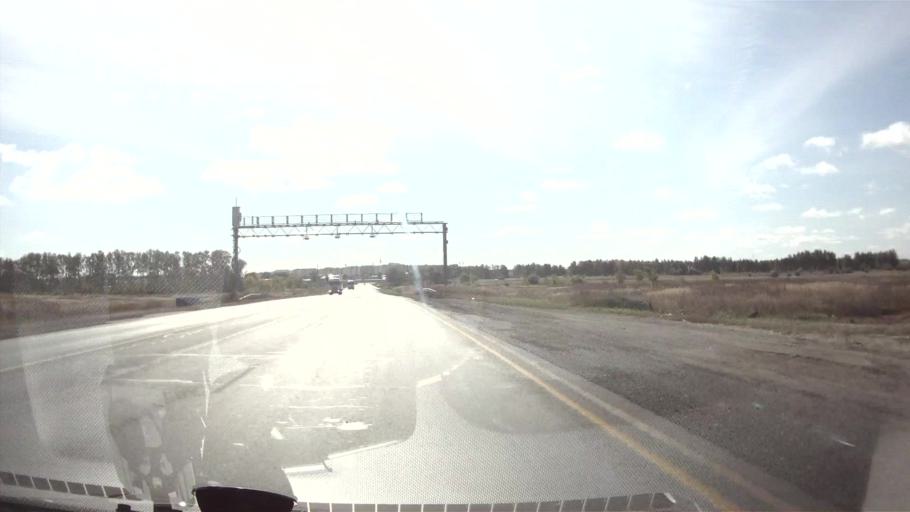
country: RU
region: Ulyanovsk
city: Isheyevka
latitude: 54.2984
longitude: 48.2470
